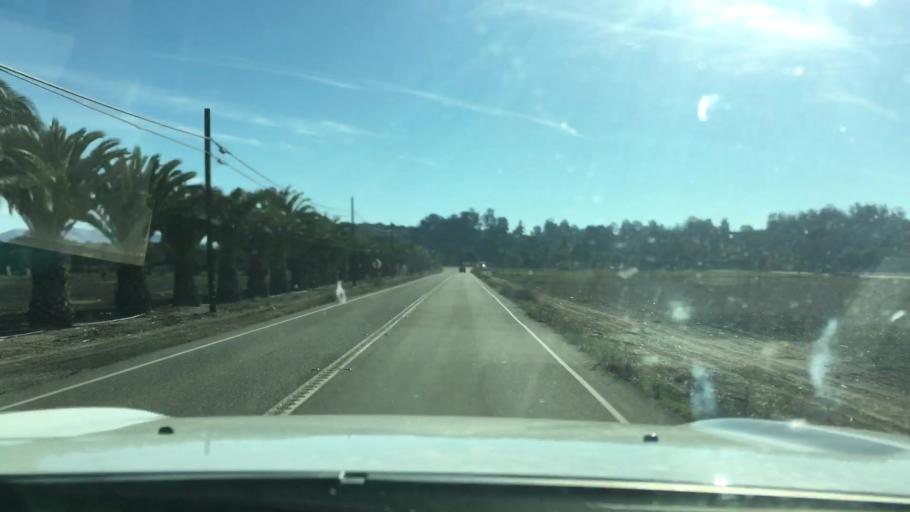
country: US
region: California
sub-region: San Luis Obispo County
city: Callender
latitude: 35.0820
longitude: -120.5513
